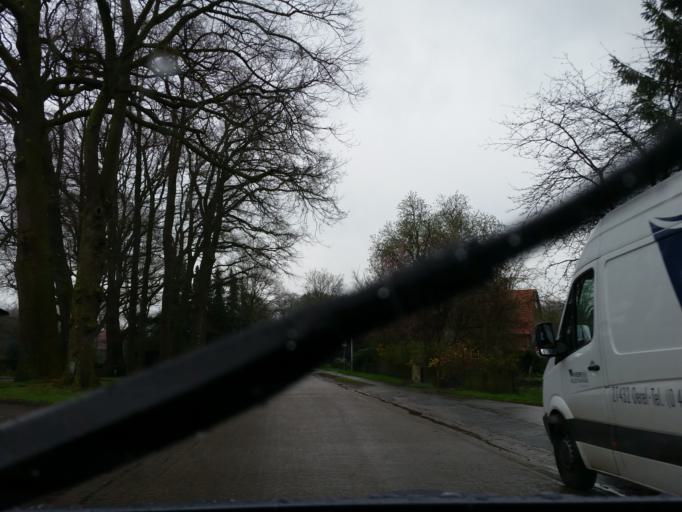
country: DE
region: Lower Saxony
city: Hipstedt
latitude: 53.4818
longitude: 8.9696
